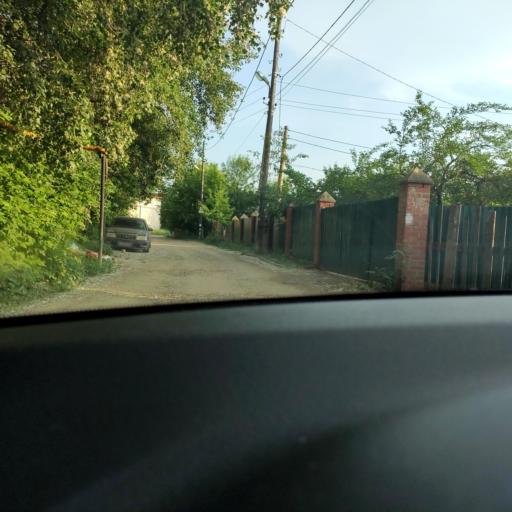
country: RU
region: Samara
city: Rozhdestveno
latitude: 53.1501
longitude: 50.0245
